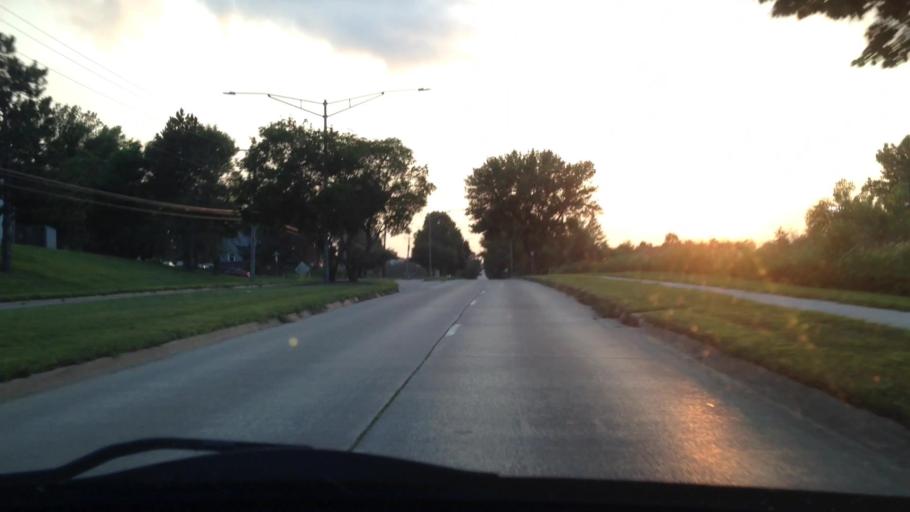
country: US
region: Iowa
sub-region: Johnson County
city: University Heights
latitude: 41.6570
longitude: -91.5762
